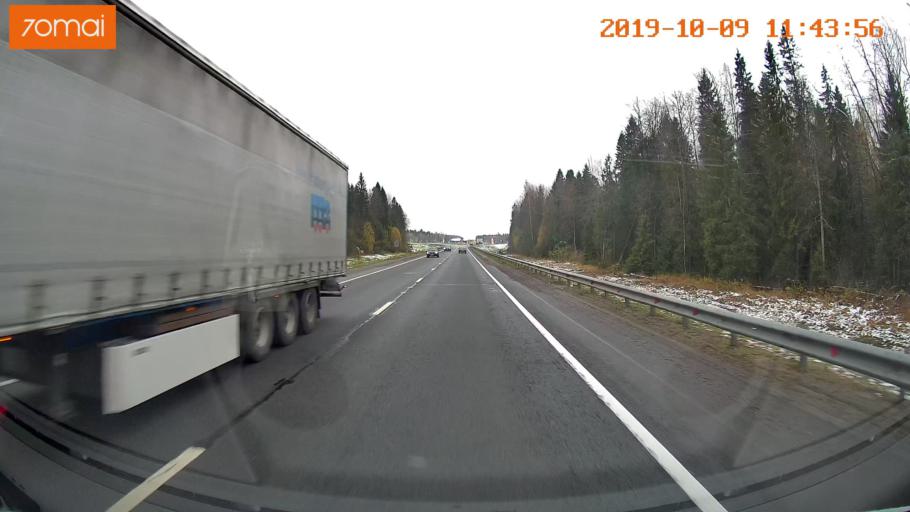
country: RU
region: Vologda
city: Gryazovets
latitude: 58.8900
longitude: 40.1886
